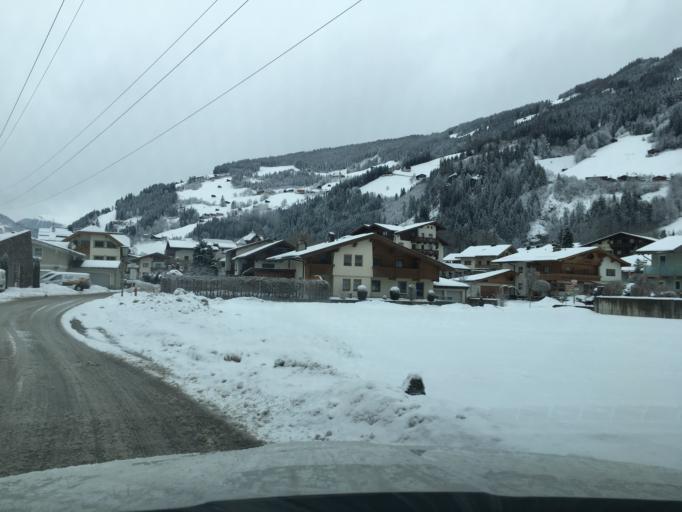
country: AT
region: Tyrol
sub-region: Politischer Bezirk Schwaz
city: Ramsau im Zillertal
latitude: 47.1952
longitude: 11.8715
